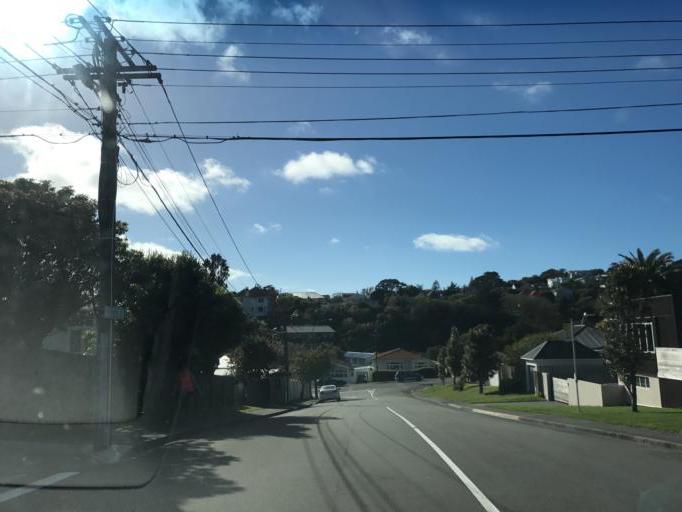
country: NZ
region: Wellington
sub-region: Wellington City
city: Kelburn
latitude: -41.2901
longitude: 174.7407
